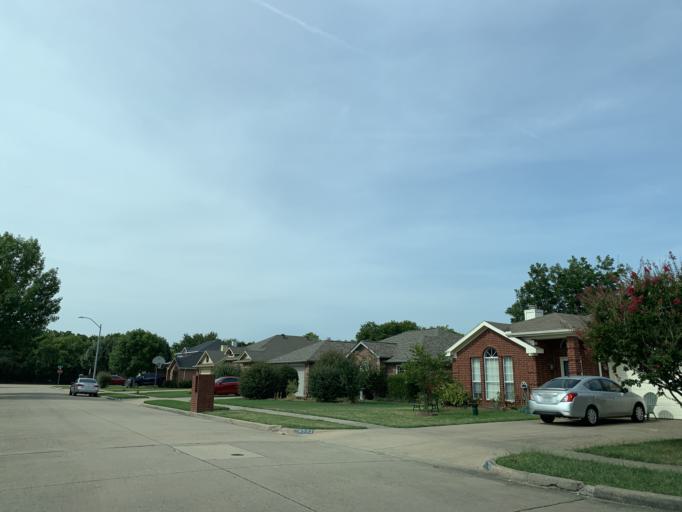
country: US
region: Texas
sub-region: Dallas County
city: Grand Prairie
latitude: 32.6594
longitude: -97.0130
